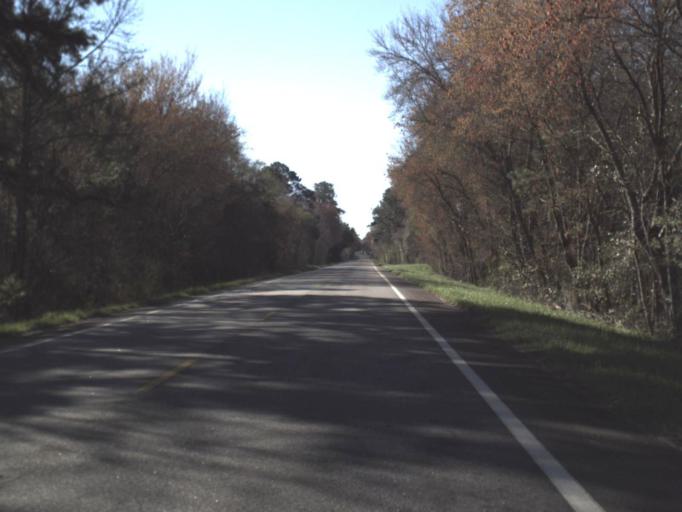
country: US
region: Georgia
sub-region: Brooks County
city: Quitman
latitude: 30.5962
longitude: -83.6424
